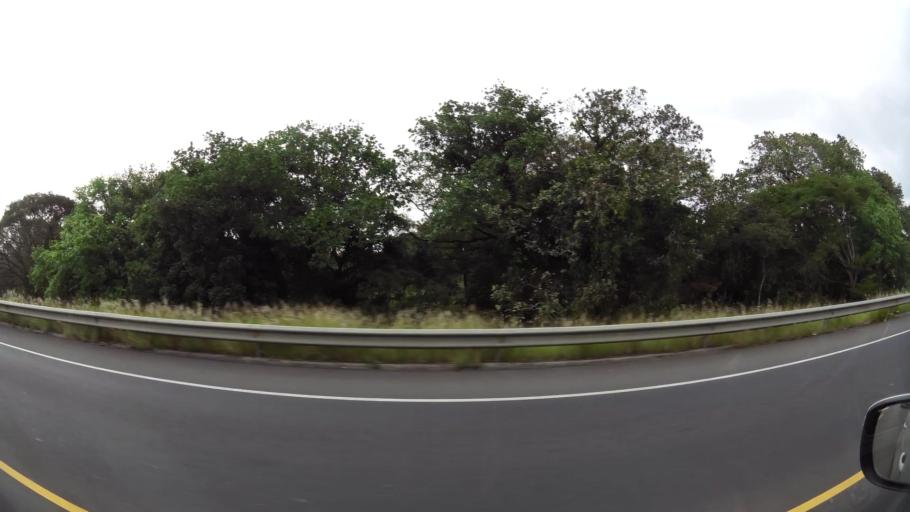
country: CR
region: Alajuela
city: Carrillos
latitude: 9.9655
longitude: -84.2976
